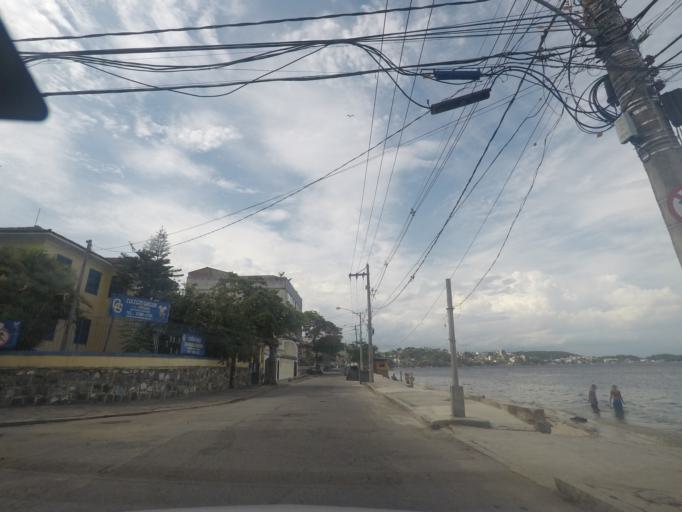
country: BR
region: Rio de Janeiro
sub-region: Rio De Janeiro
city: Rio de Janeiro
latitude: -22.8102
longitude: -43.1775
